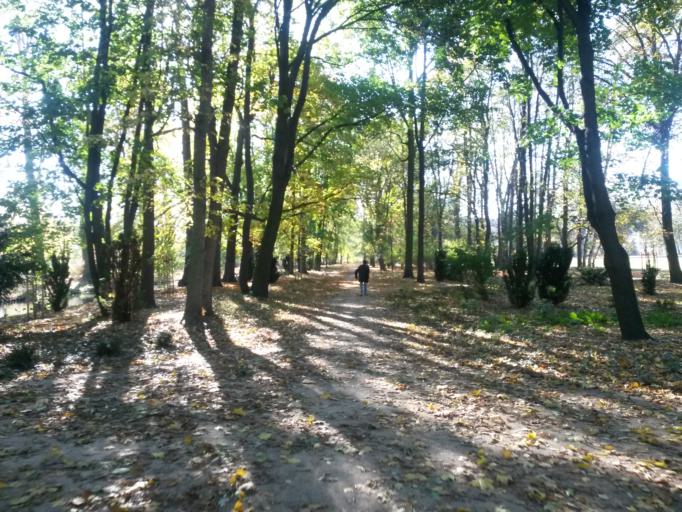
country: PL
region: Masovian Voivodeship
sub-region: Warszawa
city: Mokotow
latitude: 52.2089
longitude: 21.0347
